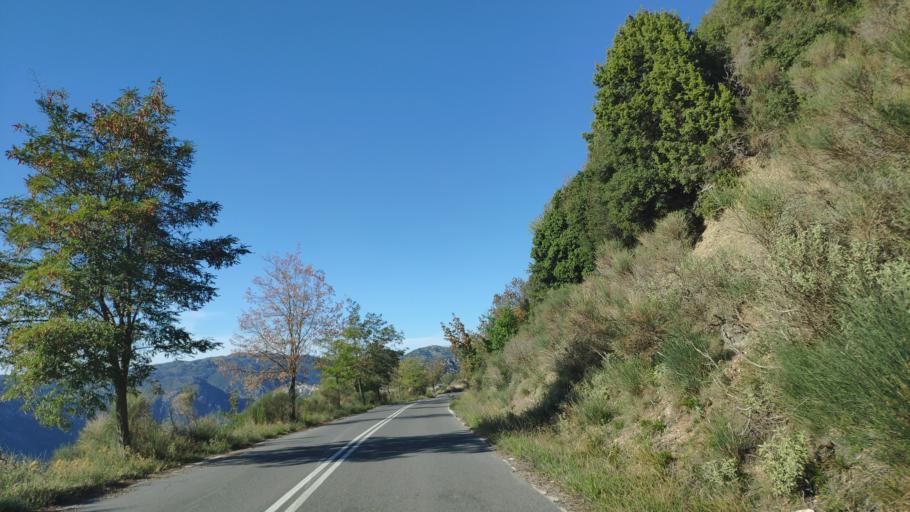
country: GR
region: Peloponnese
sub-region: Nomos Arkadias
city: Dimitsana
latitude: 37.5545
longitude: 22.0635
